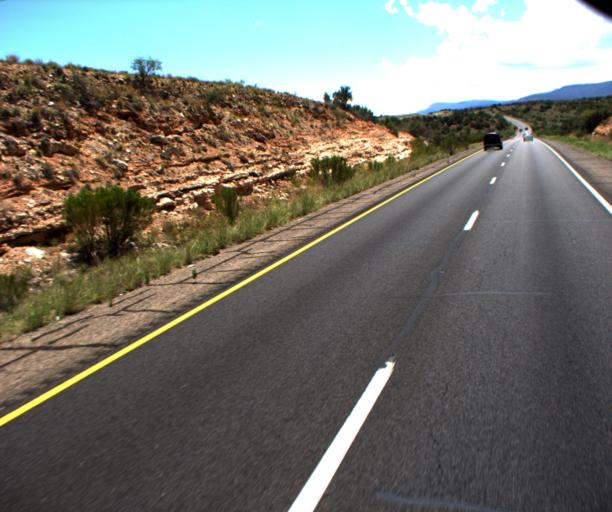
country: US
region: Arizona
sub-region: Yavapai County
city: Verde Village
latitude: 34.6722
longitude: -111.9710
